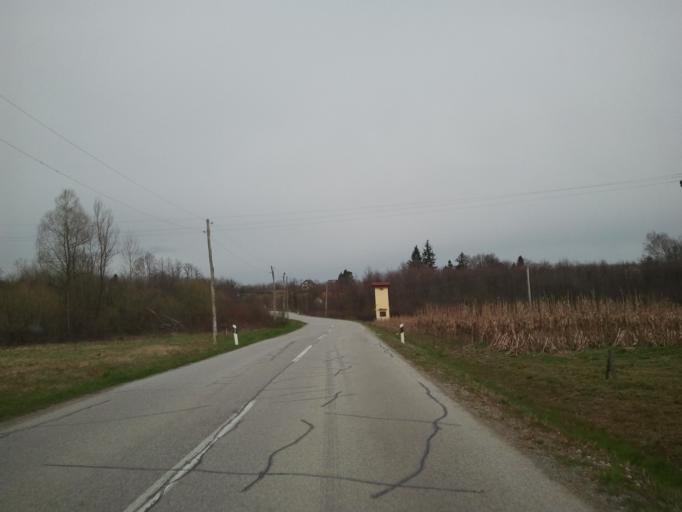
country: HR
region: Sisacko-Moslavacka
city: Gvozd
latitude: 45.3174
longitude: 15.9612
